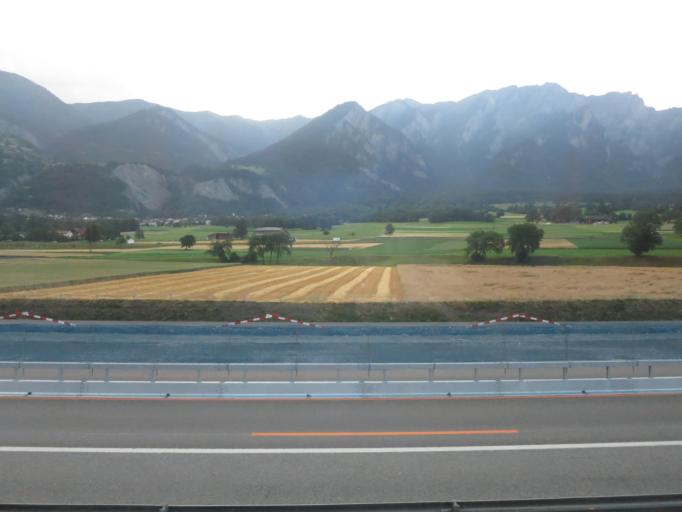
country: CH
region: Grisons
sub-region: Landquart District
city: Trimmis
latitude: 46.8991
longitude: 9.5445
